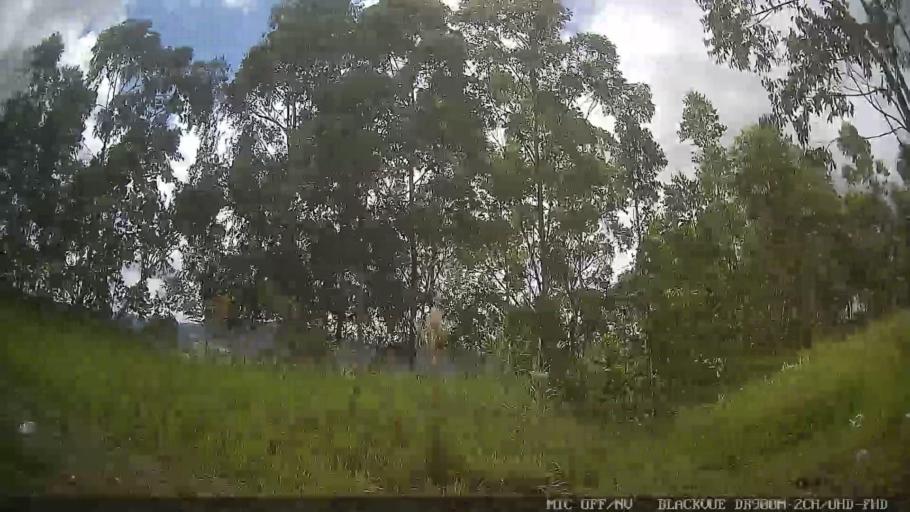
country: BR
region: Sao Paulo
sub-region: Braganca Paulista
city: Braganca Paulista
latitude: -22.8141
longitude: -46.5418
